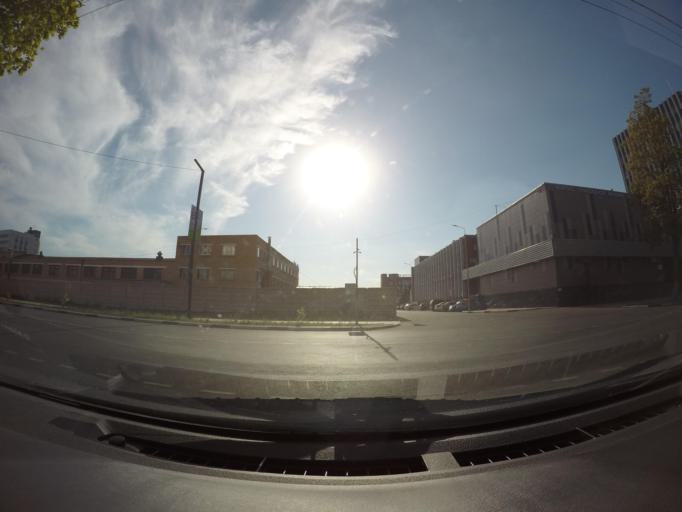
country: RU
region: Moscow
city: Severnyy
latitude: 55.9282
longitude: 37.5225
